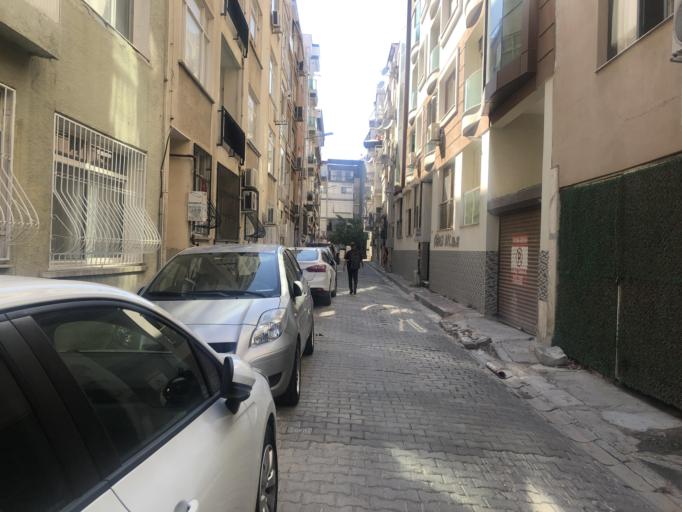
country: TR
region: Izmir
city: Karsiyaka
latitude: 38.4587
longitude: 27.1230
